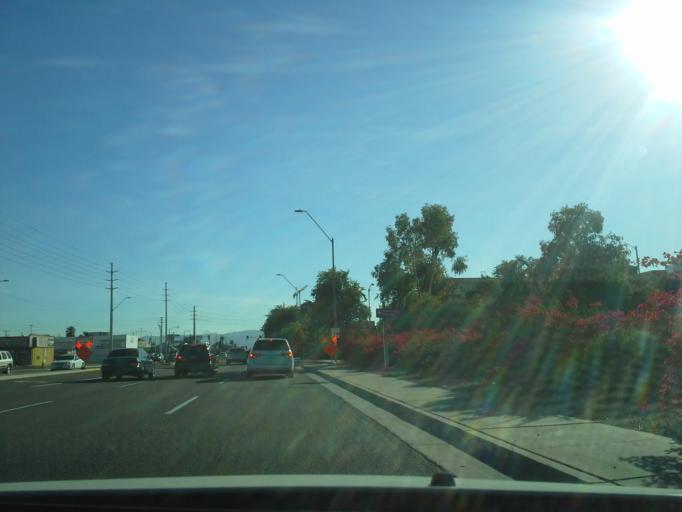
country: US
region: Arizona
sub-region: Maricopa County
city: Phoenix
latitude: 33.4606
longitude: -112.0653
